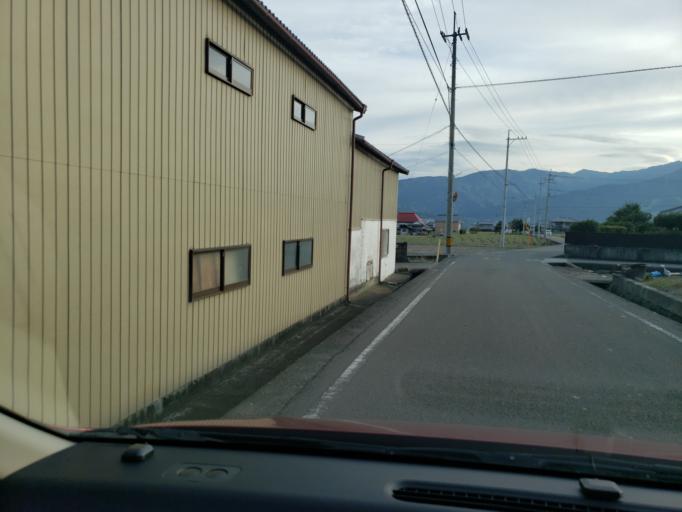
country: JP
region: Tokushima
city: Wakimachi
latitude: 34.0879
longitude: 134.2268
